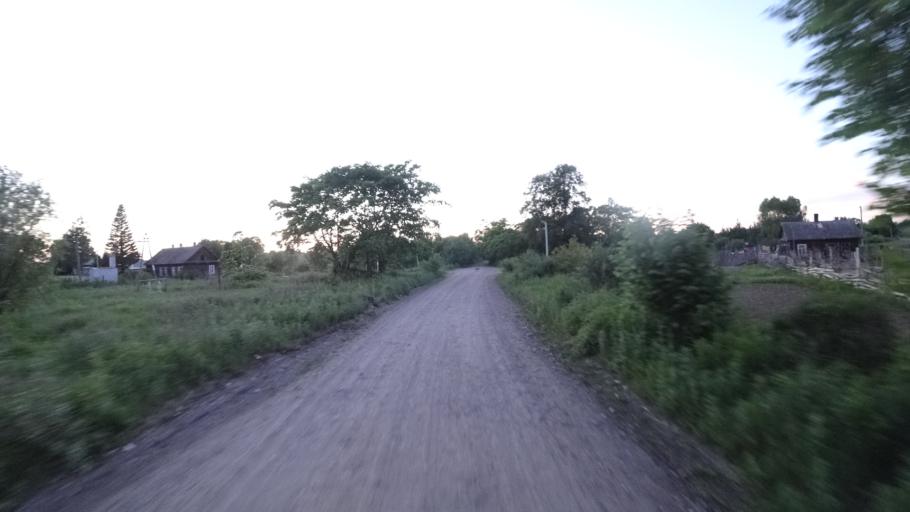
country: RU
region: Khabarovsk Krai
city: Khor
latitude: 47.8547
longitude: 134.9423
